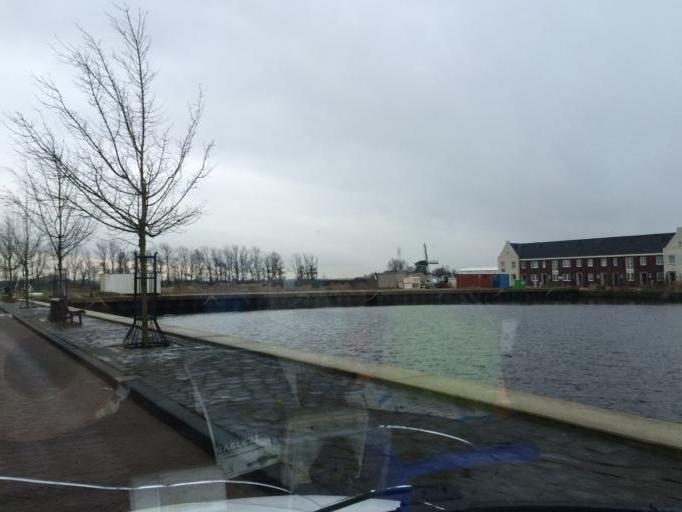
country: NL
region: North Holland
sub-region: Gemeente Haarlem
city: Haarlem
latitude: 52.4108
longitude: 4.6801
